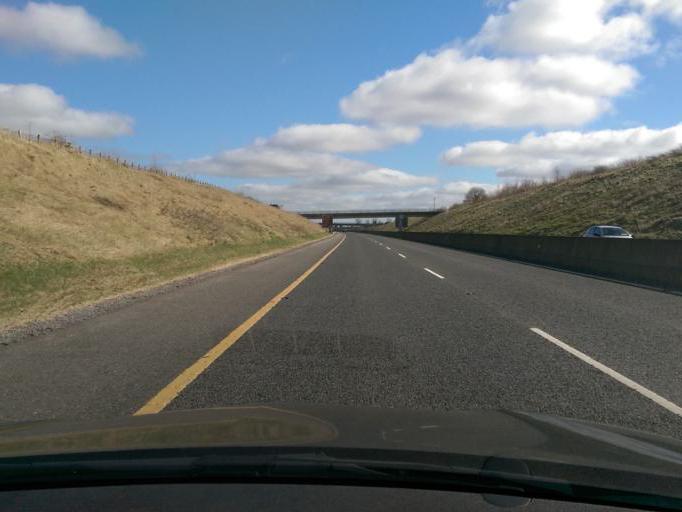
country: IE
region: Leinster
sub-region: An Iarmhi
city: Rochfortbridge
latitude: 53.3998
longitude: -7.3040
